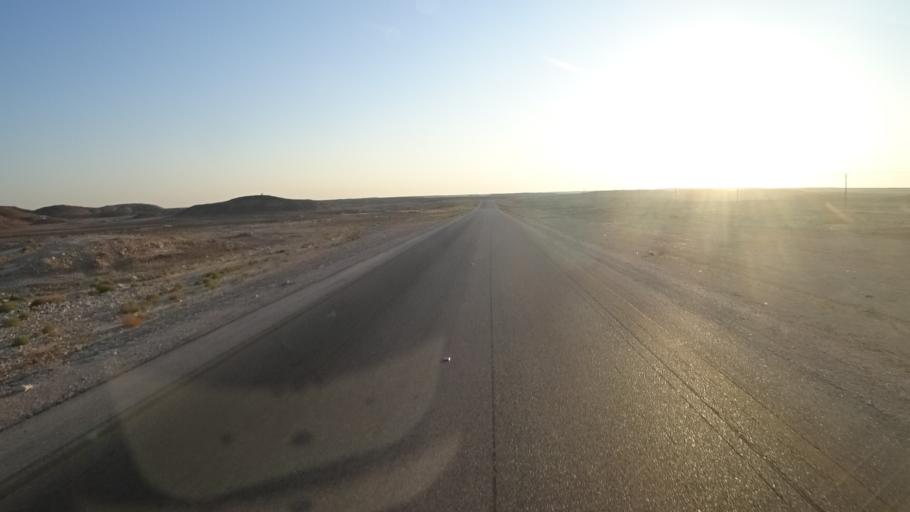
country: OM
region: Zufar
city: Salalah
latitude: 17.5304
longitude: 53.4014
